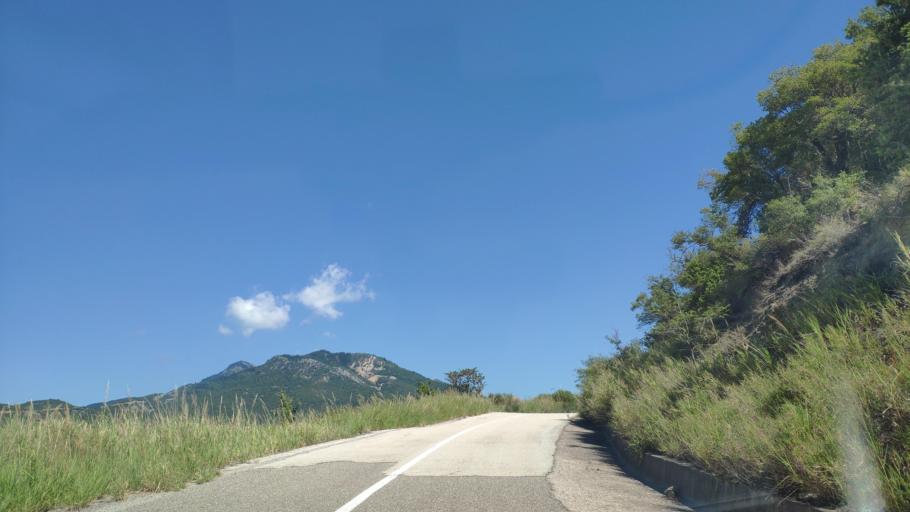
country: GR
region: Central Greece
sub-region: Nomos Evrytanias
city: Kerasochori
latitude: 39.0017
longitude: 21.5829
